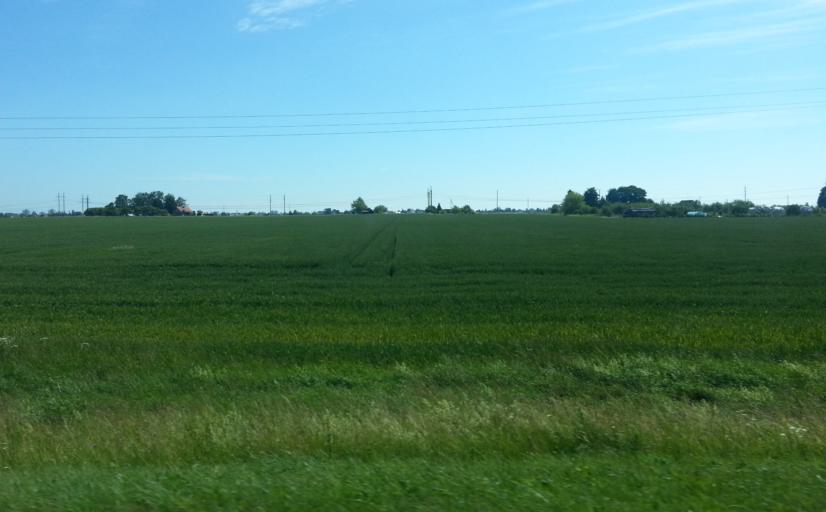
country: LT
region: Panevezys
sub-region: Panevezys City
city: Panevezys
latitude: 55.7046
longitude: 24.2719
